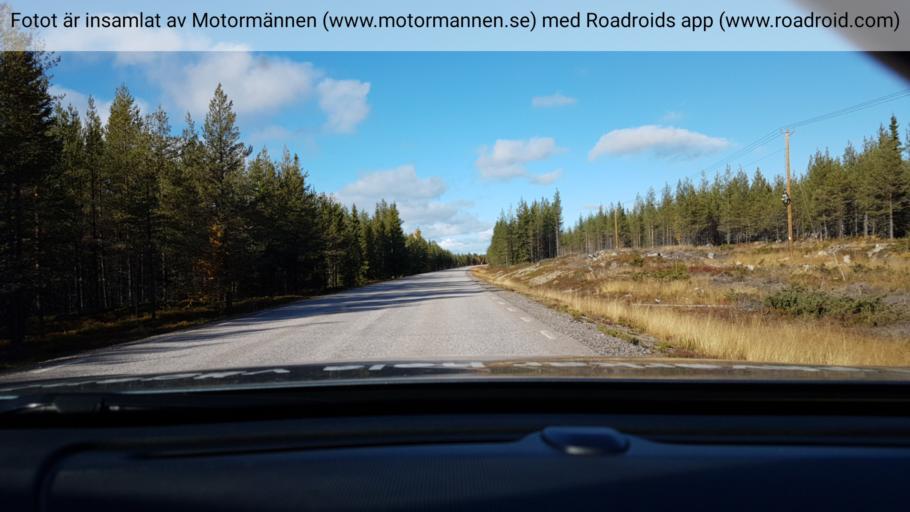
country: SE
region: Norrbotten
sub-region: Arvidsjaurs Kommun
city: Arvidsjaur
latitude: 65.7323
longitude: 18.6423
